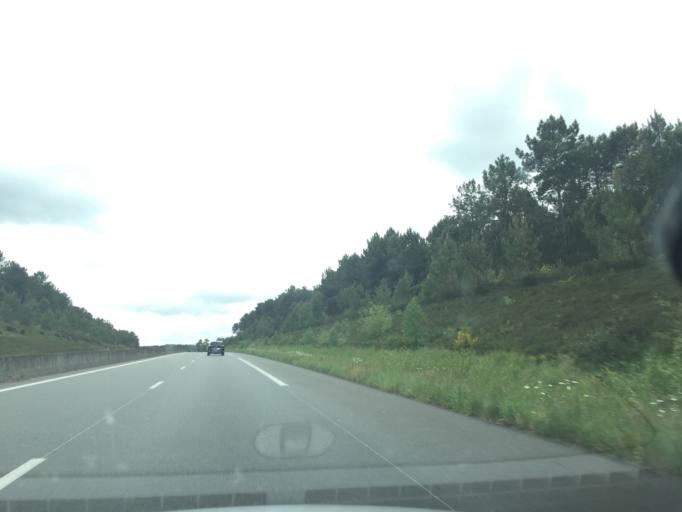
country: FR
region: Pays de la Loire
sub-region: Departement de la Sarthe
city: Mayet
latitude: 47.7541
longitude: 0.3147
